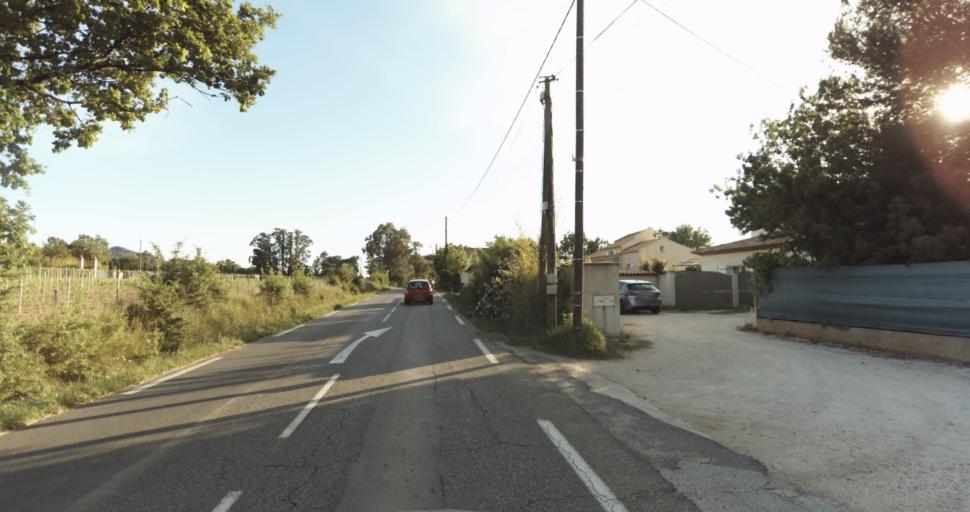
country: FR
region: Provence-Alpes-Cote d'Azur
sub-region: Departement du Var
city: La Crau
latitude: 43.1655
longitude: 6.1049
